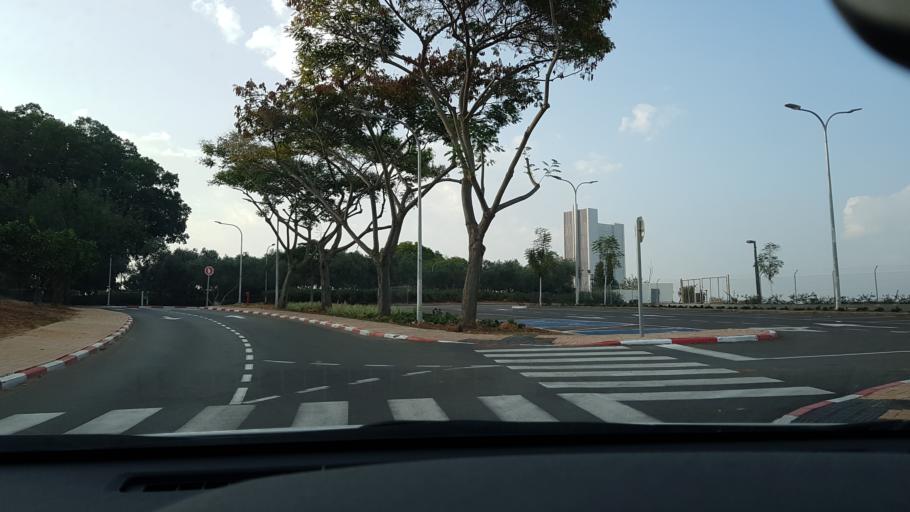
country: IL
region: Central District
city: Ness Ziona
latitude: 31.9083
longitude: 34.8202
